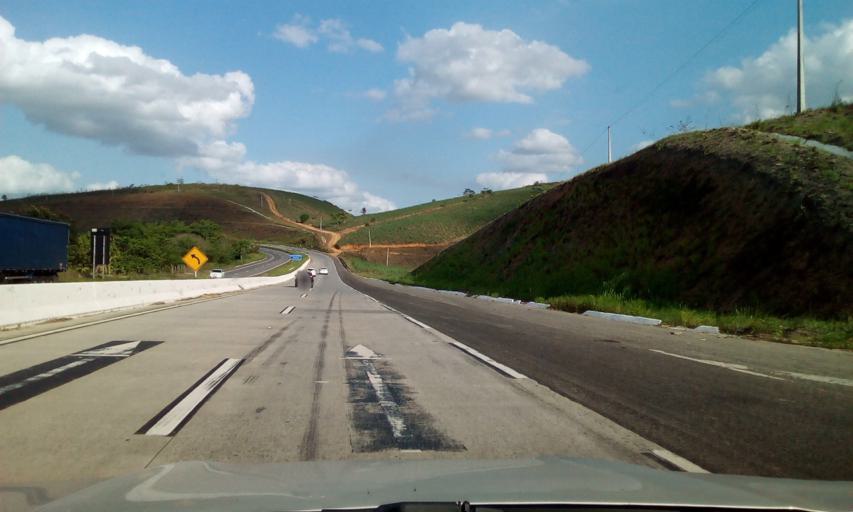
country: BR
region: Pernambuco
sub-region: Gameleira
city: Gameleira
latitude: -8.5536
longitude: -35.4538
